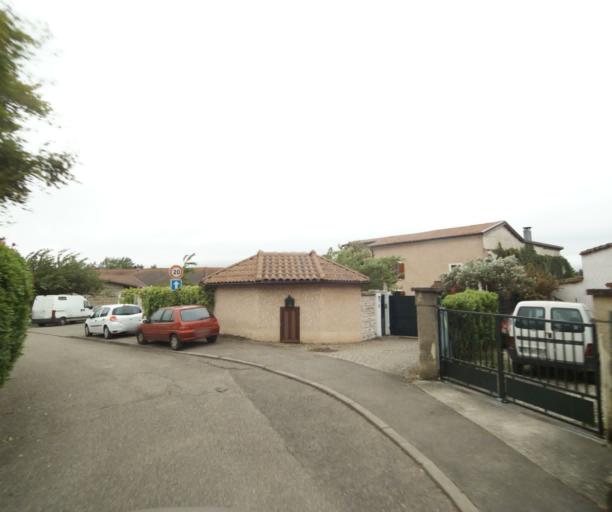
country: FR
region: Rhone-Alpes
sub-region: Departement de l'Ain
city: Miribel
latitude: 45.8298
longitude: 4.9437
